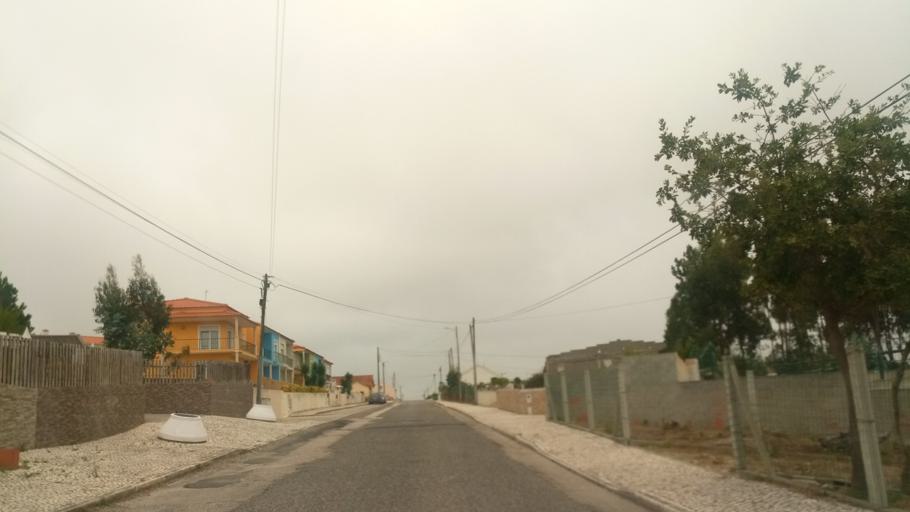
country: PT
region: Leiria
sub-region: Caldas da Rainha
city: Caldas da Rainha
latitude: 39.4285
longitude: -9.1543
